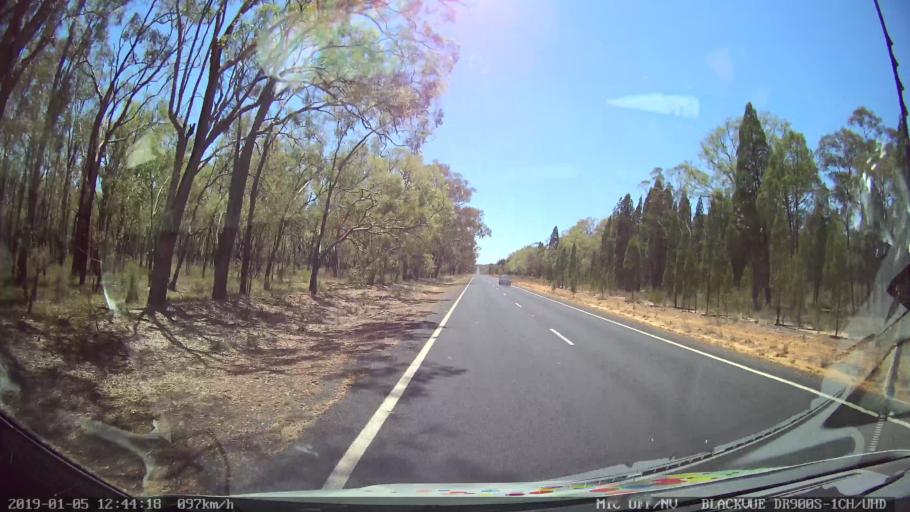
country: AU
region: New South Wales
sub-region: Warrumbungle Shire
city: Coonabarabran
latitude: -31.1391
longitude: 149.5355
